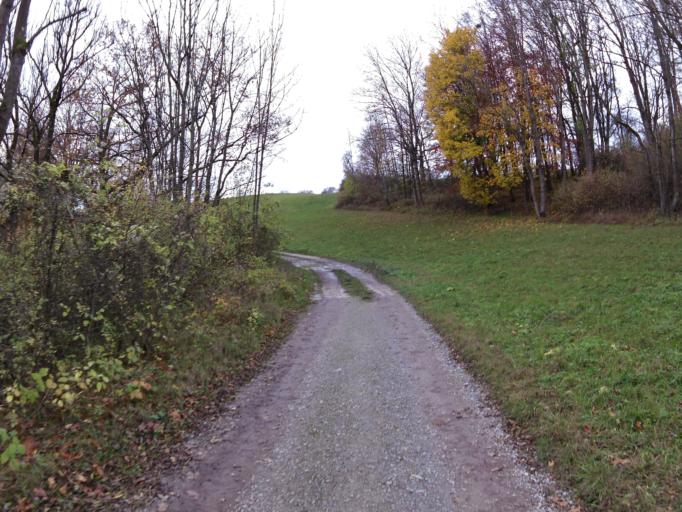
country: DE
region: Thuringia
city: Bischofroda
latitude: 51.0759
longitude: 10.3776
